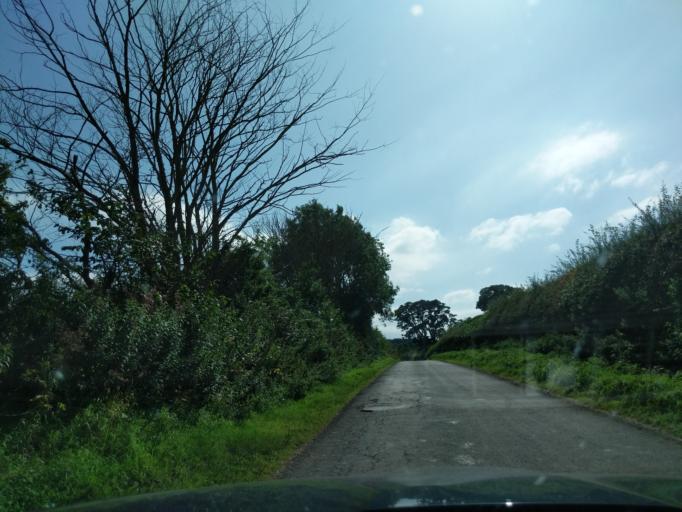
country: GB
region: England
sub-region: Northumberland
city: Ford
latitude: 55.6391
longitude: -2.1375
